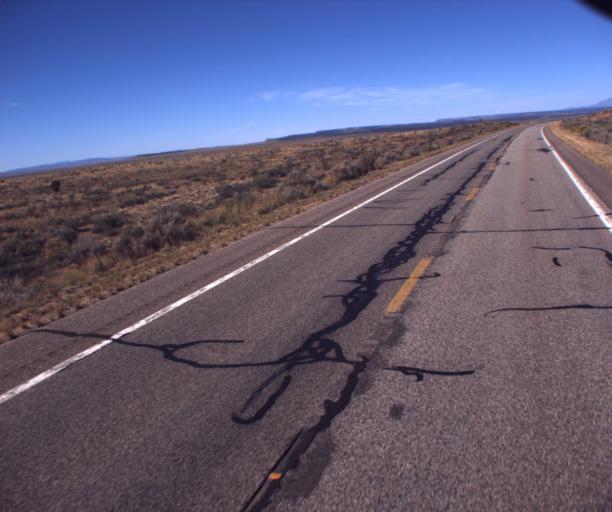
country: US
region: Arizona
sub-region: Mohave County
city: Colorado City
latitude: 36.8844
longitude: -112.9026
